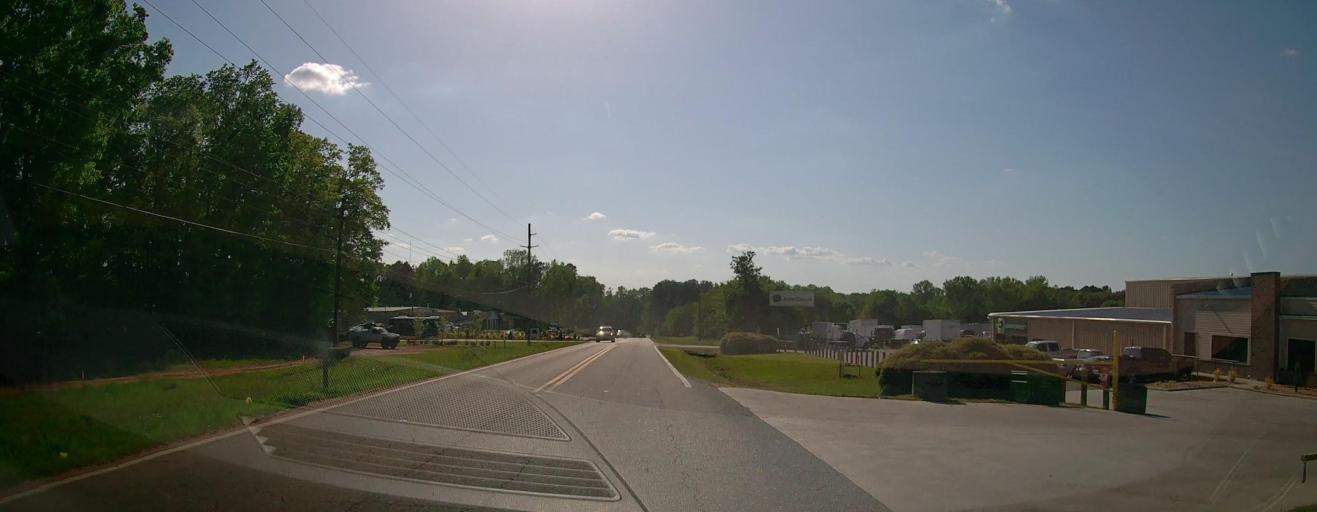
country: US
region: Georgia
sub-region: Morgan County
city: Madison
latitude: 33.5639
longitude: -83.4842
